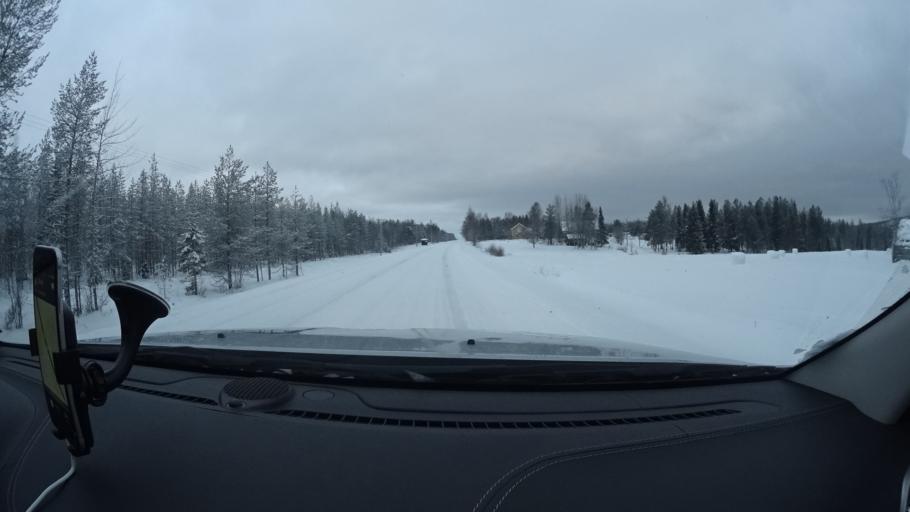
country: FI
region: Lapland
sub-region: Itae-Lappi
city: Kemijaervi
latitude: 66.2941
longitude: 27.1357
